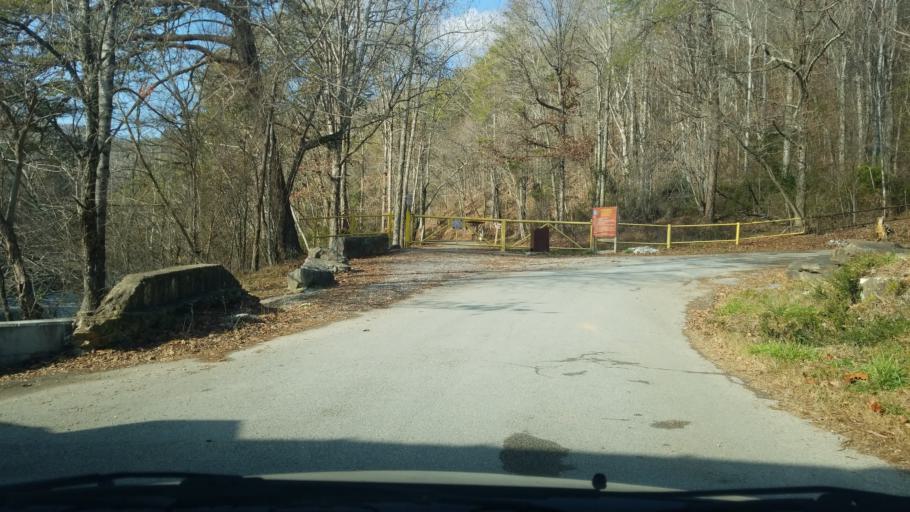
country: US
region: Tennessee
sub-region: Hamilton County
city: Soddy-Daisy
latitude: 35.3017
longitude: -85.1665
